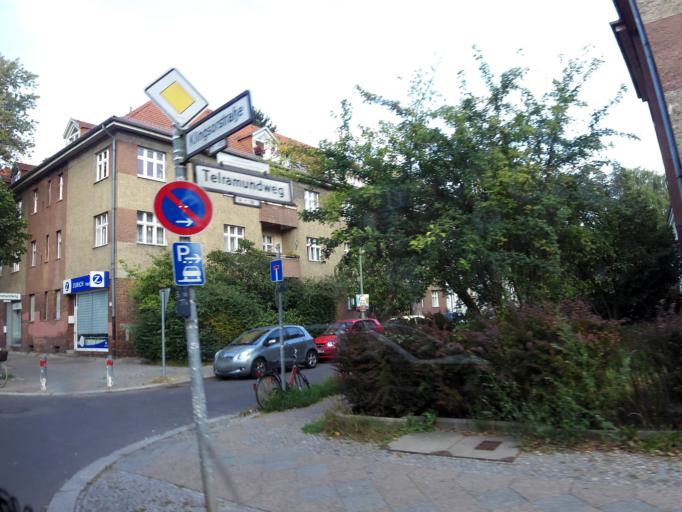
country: DE
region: Berlin
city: Steglitz Bezirk
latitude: 52.4464
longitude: 13.3254
